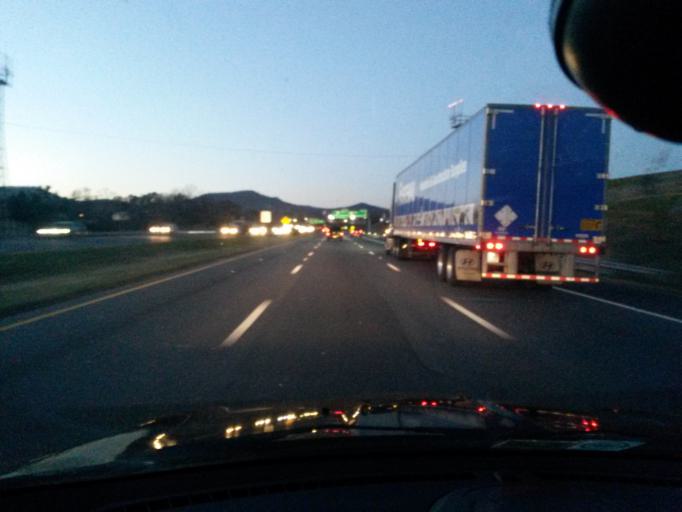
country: US
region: Virginia
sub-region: Roanoke County
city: Hollins
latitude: 37.3210
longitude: -79.9848
